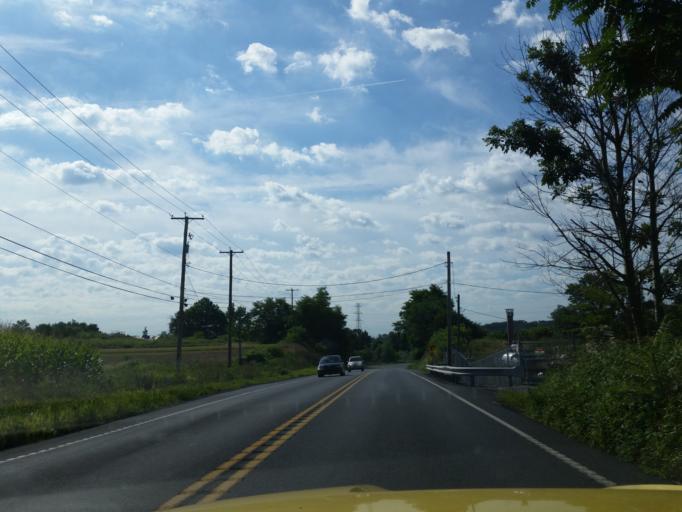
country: US
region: Pennsylvania
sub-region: Lebanon County
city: Sand Hill
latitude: 40.3870
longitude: -76.4127
